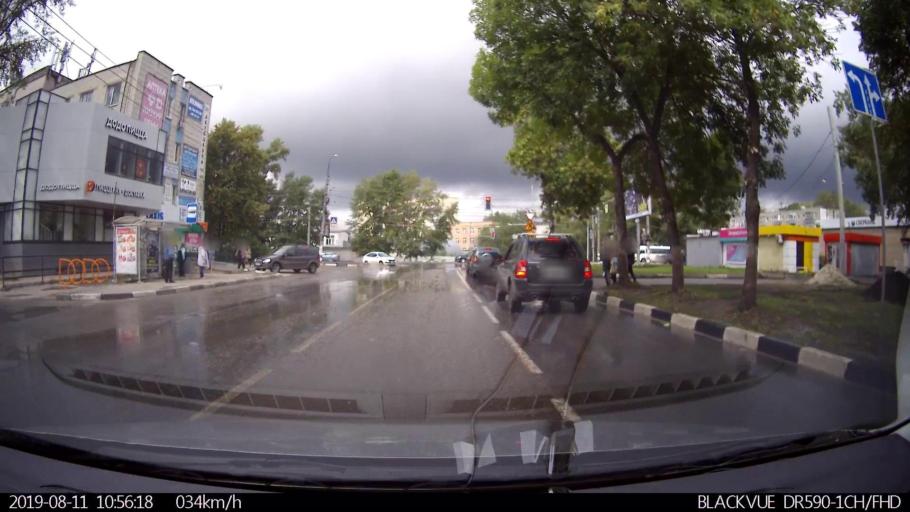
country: RU
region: Ulyanovsk
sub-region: Ulyanovskiy Rayon
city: Ulyanovsk
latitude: 54.2575
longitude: 48.3221
